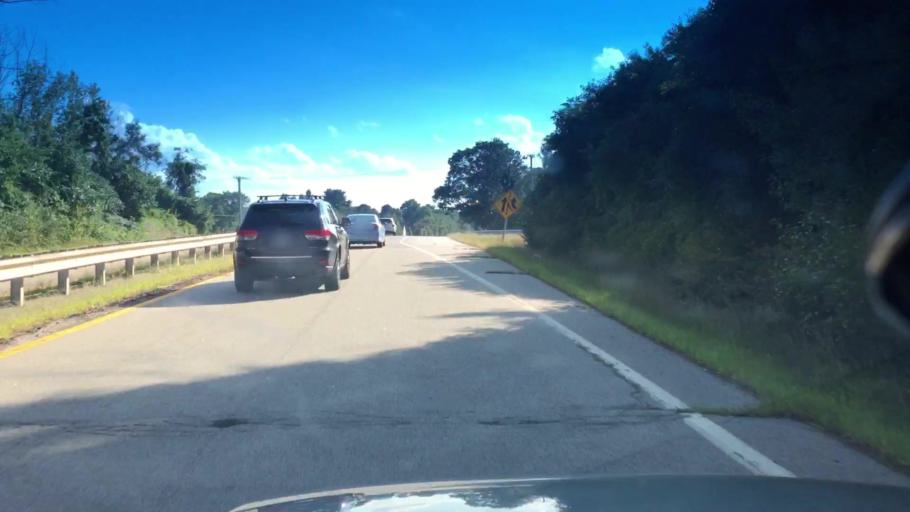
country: US
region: Maine
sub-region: York County
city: Kittery
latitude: 43.1025
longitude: -70.7444
